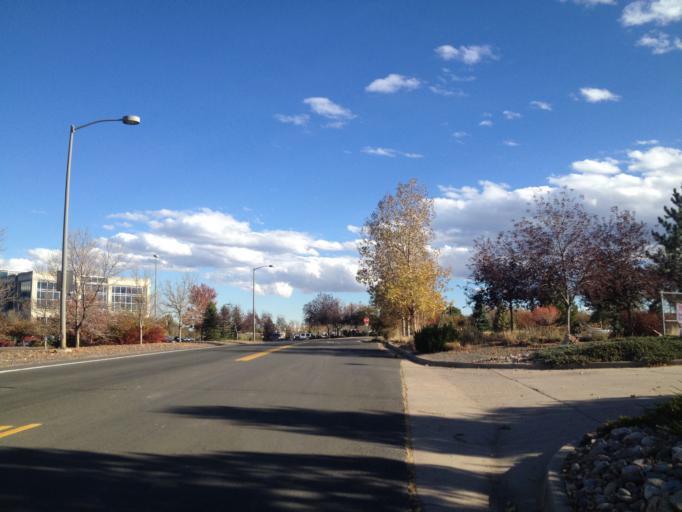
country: US
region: Colorado
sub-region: Broomfield County
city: Broomfield
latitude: 39.9141
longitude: -105.1085
